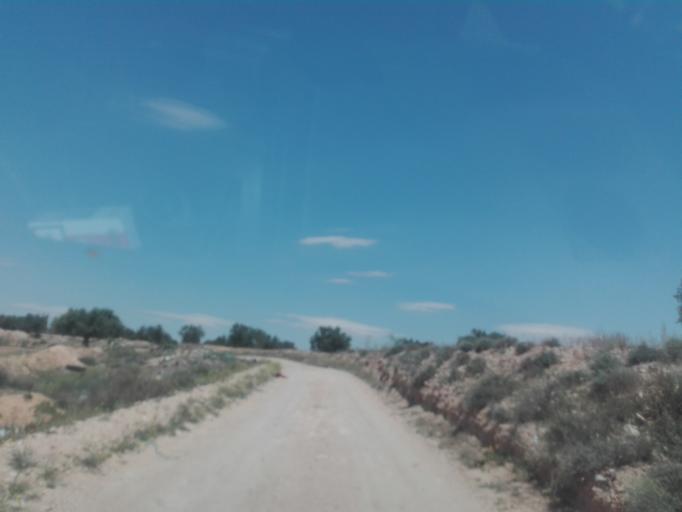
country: TN
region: Safaqis
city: Sfax
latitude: 34.6793
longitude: 10.6120
